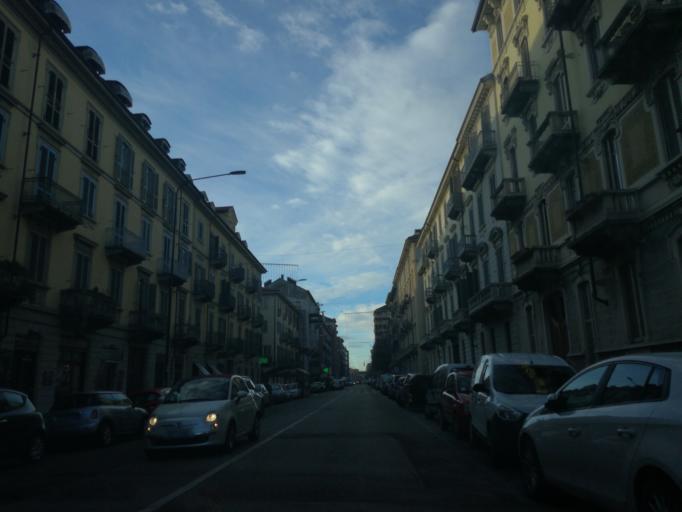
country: IT
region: Piedmont
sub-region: Provincia di Torino
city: Turin
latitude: 45.0752
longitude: 7.6636
